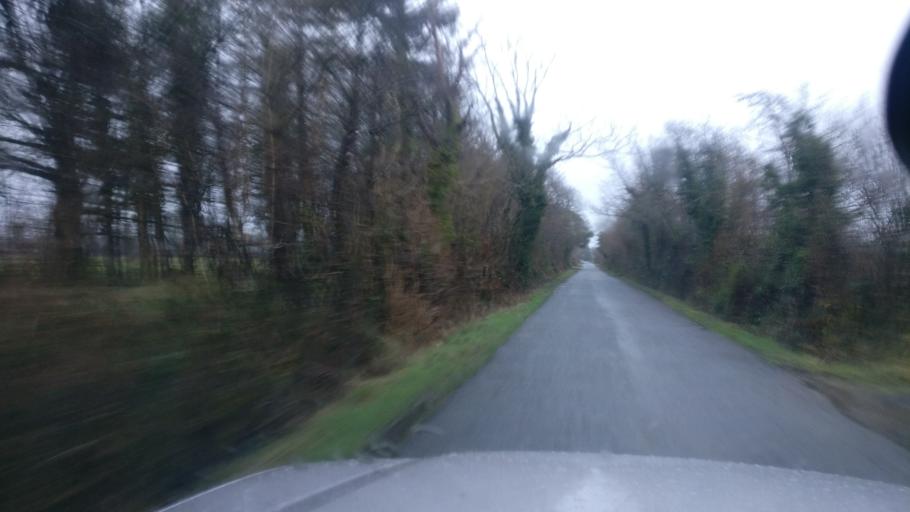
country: IE
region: Connaught
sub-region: County Galway
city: Ballinasloe
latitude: 53.3194
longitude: -8.3762
